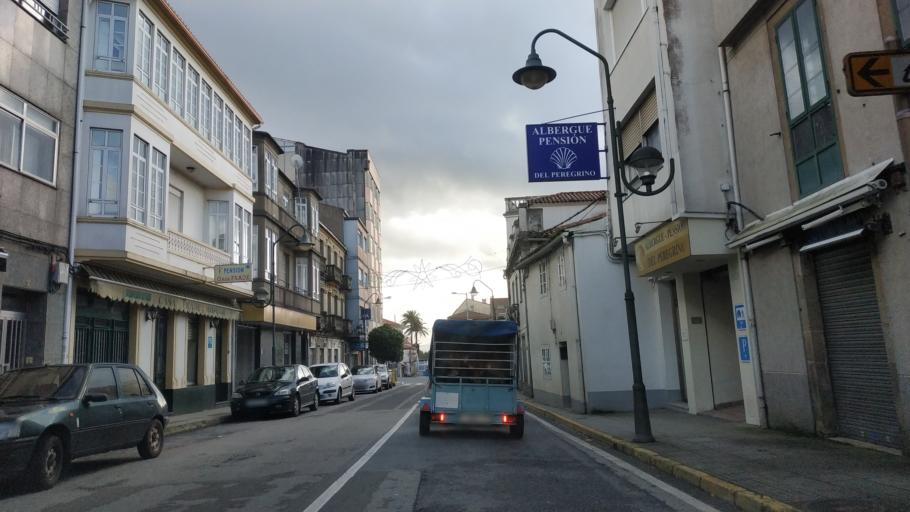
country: ES
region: Galicia
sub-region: Provincia da Coruna
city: Arzua
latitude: 42.9274
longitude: -8.1639
